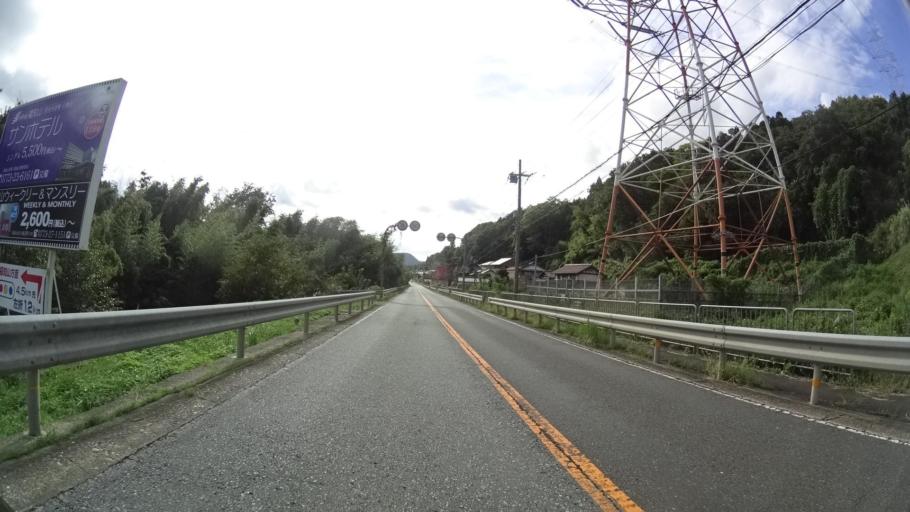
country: JP
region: Kyoto
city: Ayabe
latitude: 35.2930
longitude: 135.3077
